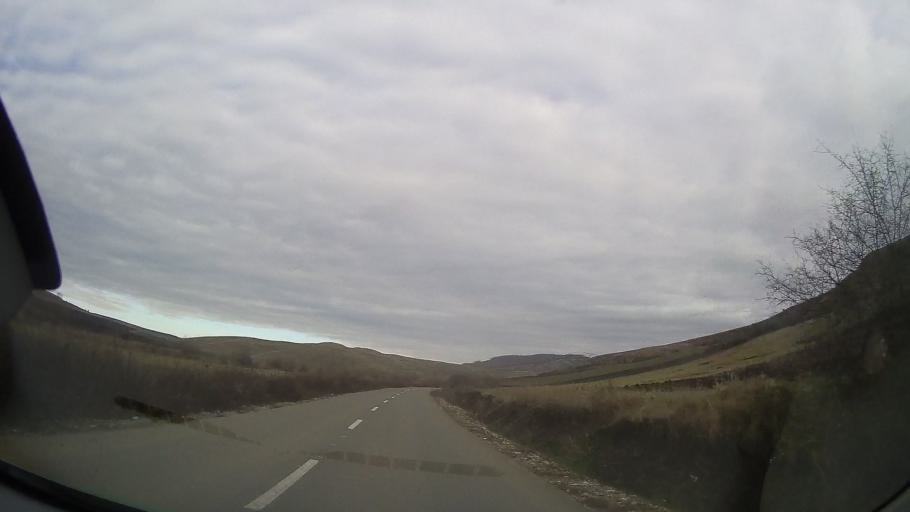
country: RO
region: Bistrita-Nasaud
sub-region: Comuna Silvasu de Campie
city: Silvasu de Campie
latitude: 46.7993
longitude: 24.2964
